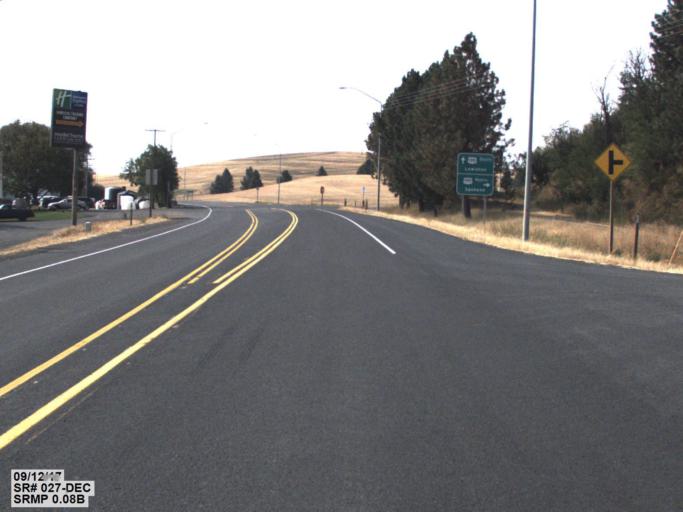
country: US
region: Washington
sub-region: Whitman County
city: Pullman
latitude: 46.7091
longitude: -117.2026
